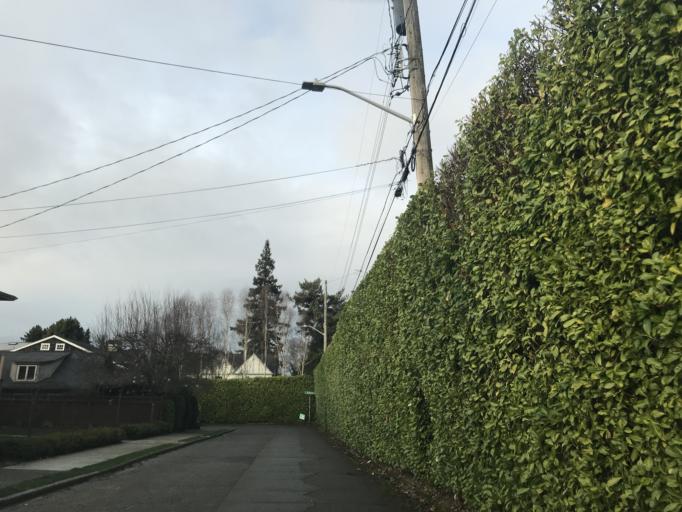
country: US
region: Washington
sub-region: King County
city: Seattle
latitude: 47.6291
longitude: -122.2895
